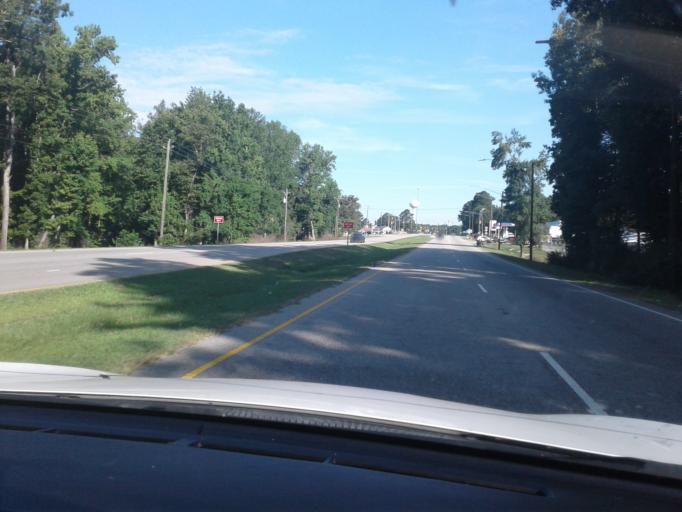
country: US
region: North Carolina
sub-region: Harnett County
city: Erwin
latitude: 35.3336
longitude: -78.6707
